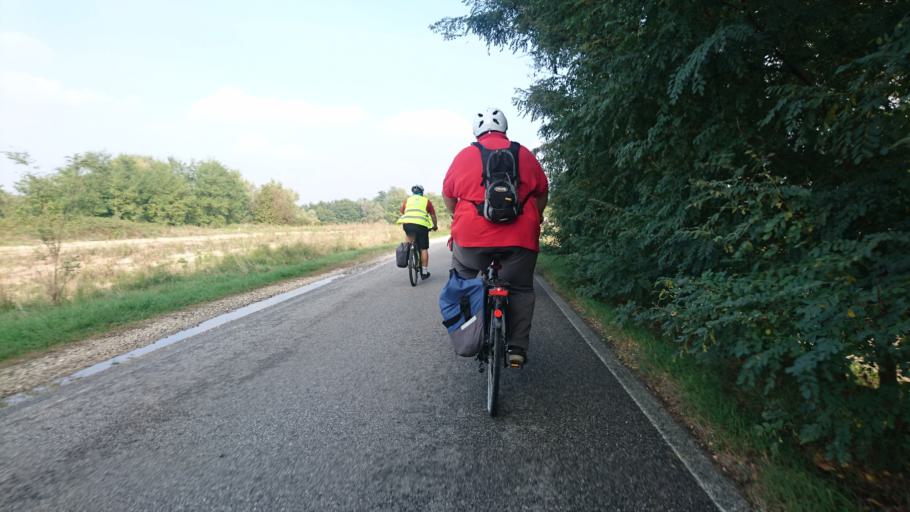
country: IT
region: Veneto
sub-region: Provincia di Rovigo
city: Arqua Polesine
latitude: 44.9976
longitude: 11.7375
